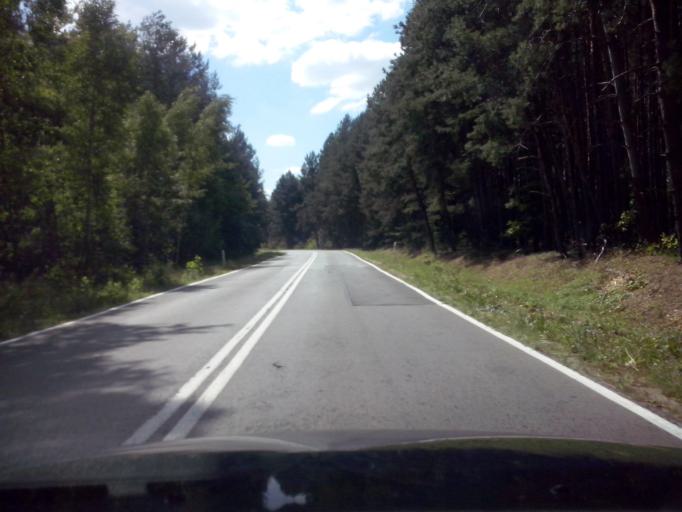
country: PL
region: Swietokrzyskie
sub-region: Powiat staszowski
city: Szydlow
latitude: 50.6221
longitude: 21.0172
